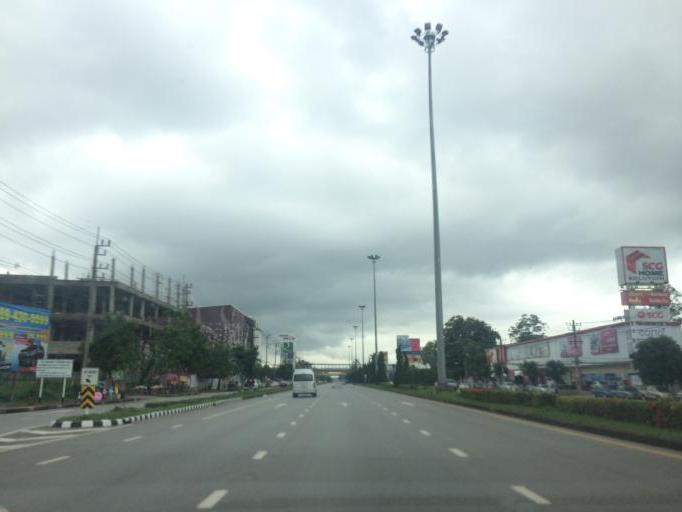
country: TH
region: Chiang Rai
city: Chiang Rai
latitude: 19.8839
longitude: 99.8346
